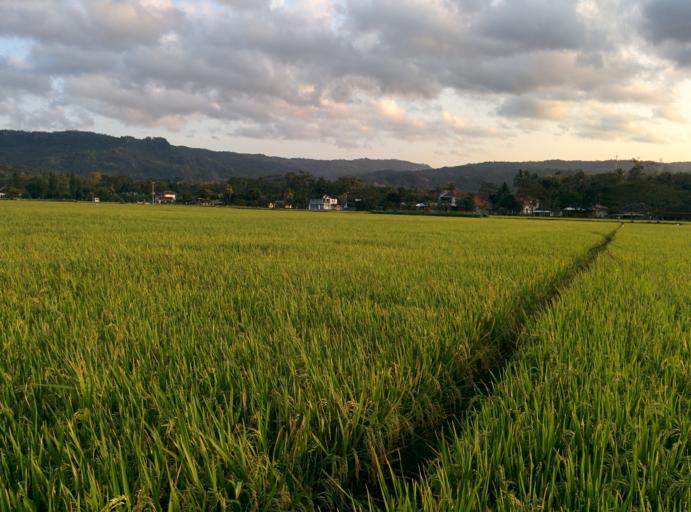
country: ID
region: East Java
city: Sitiarjo
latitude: -8.3817
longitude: 112.6793
